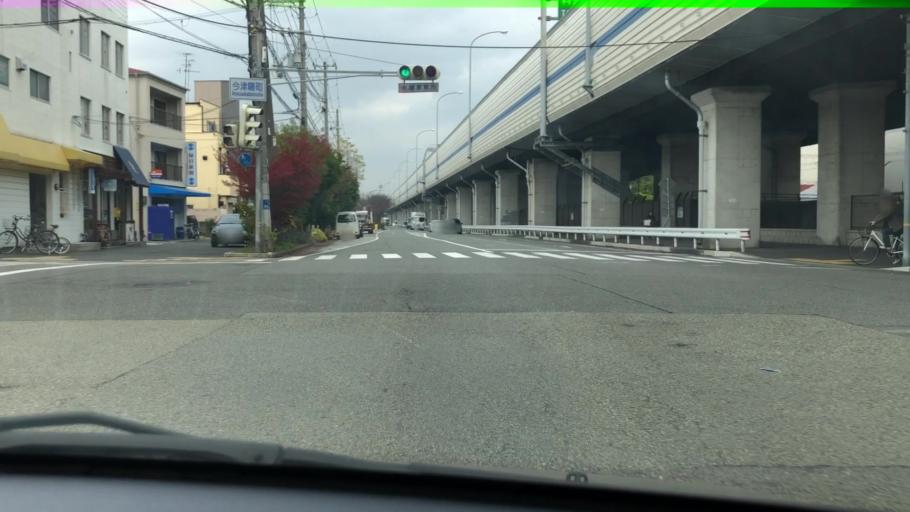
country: JP
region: Hyogo
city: Nishinomiya-hama
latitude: 34.7288
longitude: 135.3573
